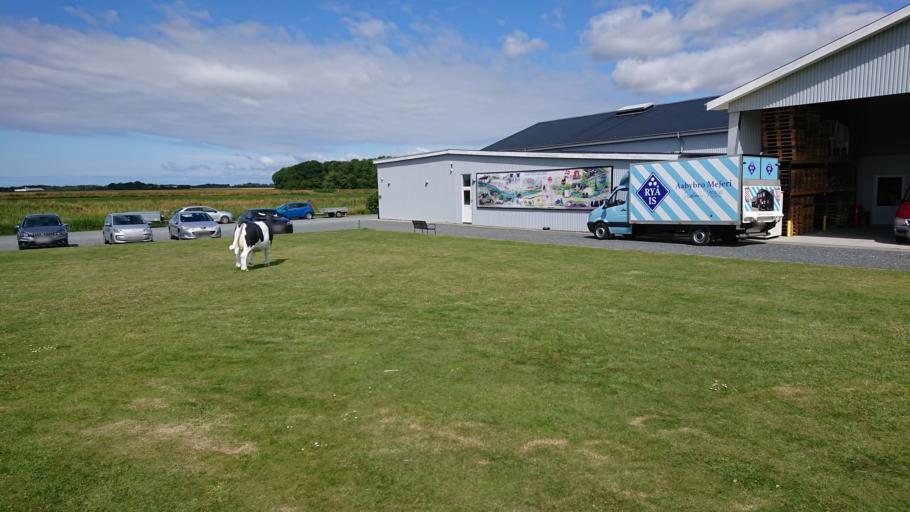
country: DK
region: North Denmark
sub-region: Jammerbugt Kommune
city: Abybro
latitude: 57.1676
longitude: 9.7166
